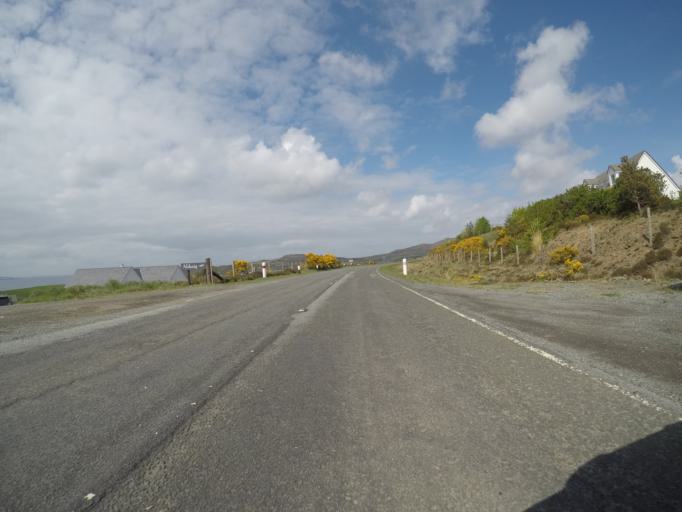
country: GB
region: Scotland
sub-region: Highland
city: Portree
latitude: 57.5735
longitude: -6.3650
